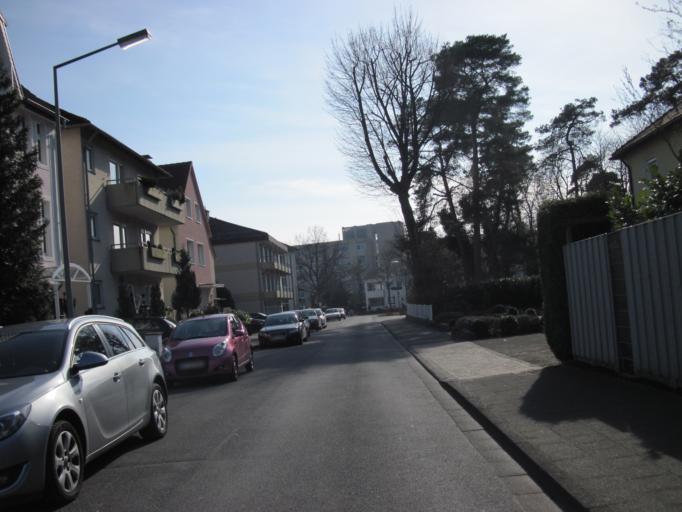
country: DE
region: North Rhine-Westphalia
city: Bad Lippspringe
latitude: 51.7888
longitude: 8.8192
